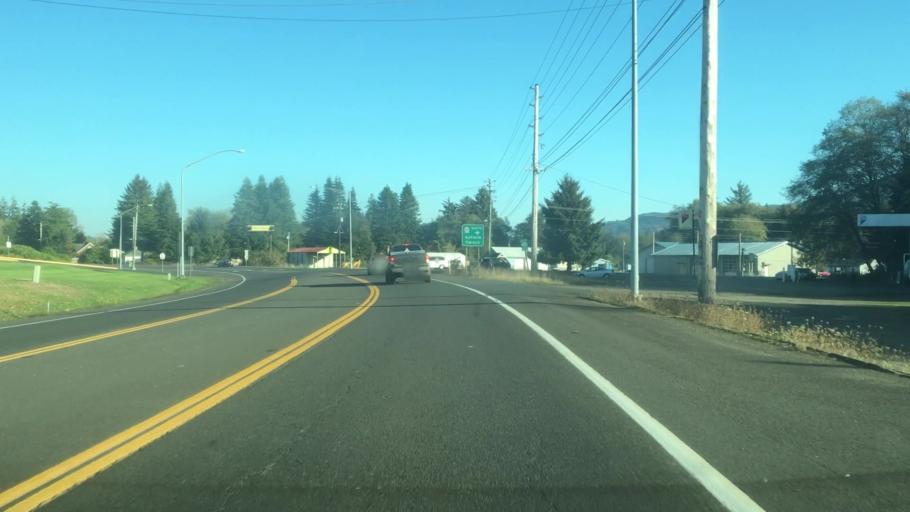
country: US
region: Oregon
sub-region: Clatsop County
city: Astoria
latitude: 46.3762
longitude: -123.8039
